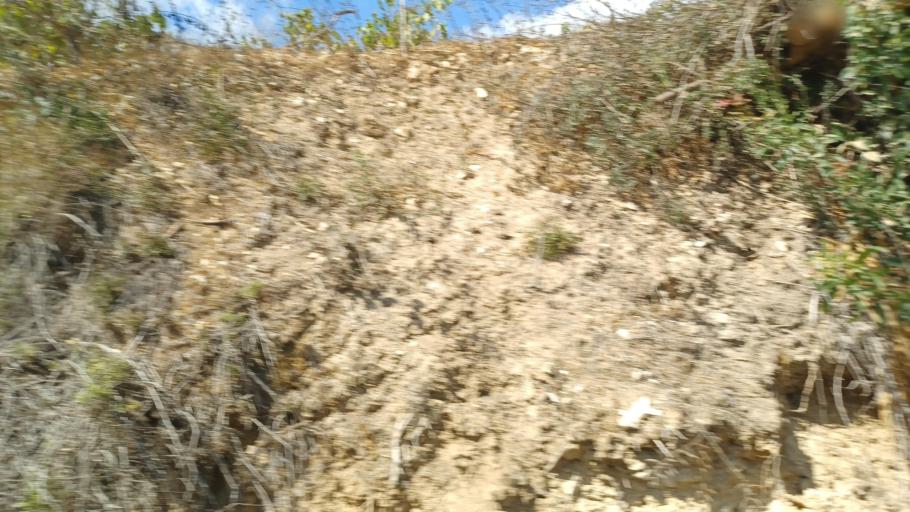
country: CY
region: Pafos
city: Tala
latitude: 34.8698
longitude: 32.4544
